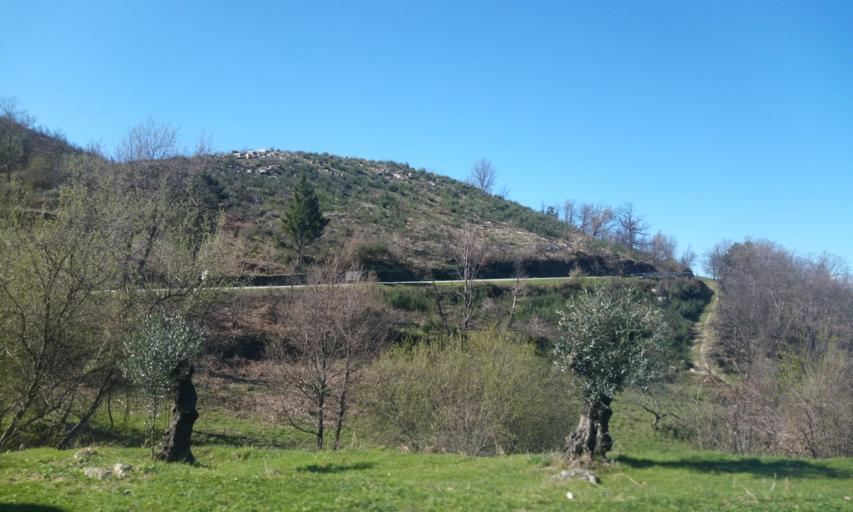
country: PT
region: Guarda
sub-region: Manteigas
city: Manteigas
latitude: 40.4626
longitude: -7.6095
